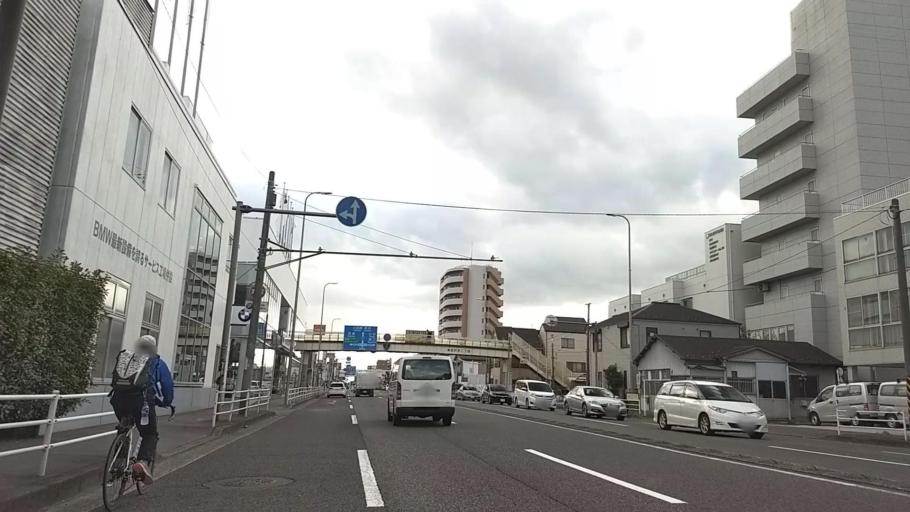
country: JP
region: Kanagawa
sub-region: Kawasaki-shi
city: Kawasaki
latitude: 35.5464
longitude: 139.6923
